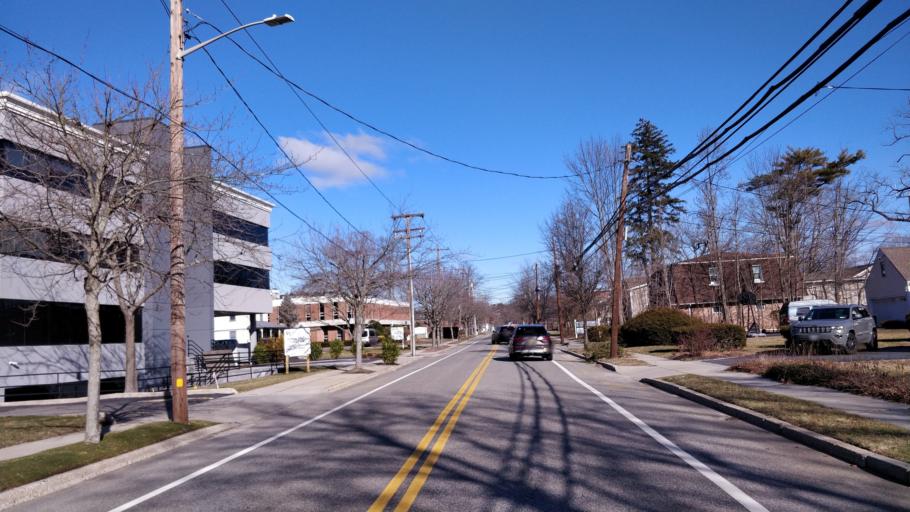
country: US
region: New York
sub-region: Suffolk County
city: Smithtown
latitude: 40.8514
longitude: -73.1974
